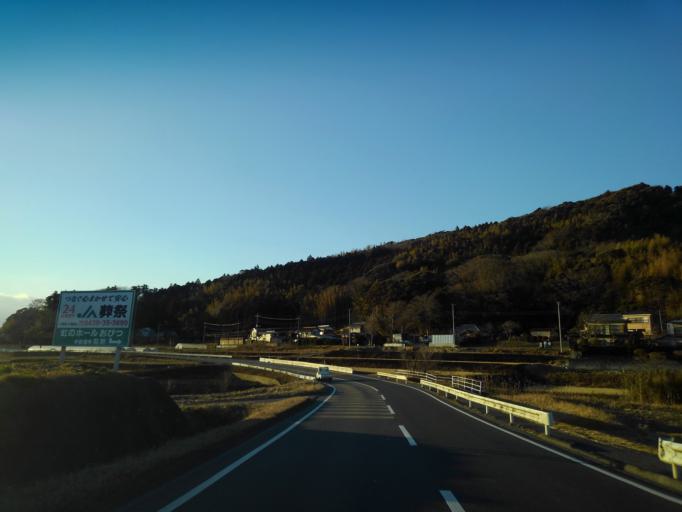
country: JP
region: Chiba
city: Kisarazu
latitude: 35.3062
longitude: 139.9846
